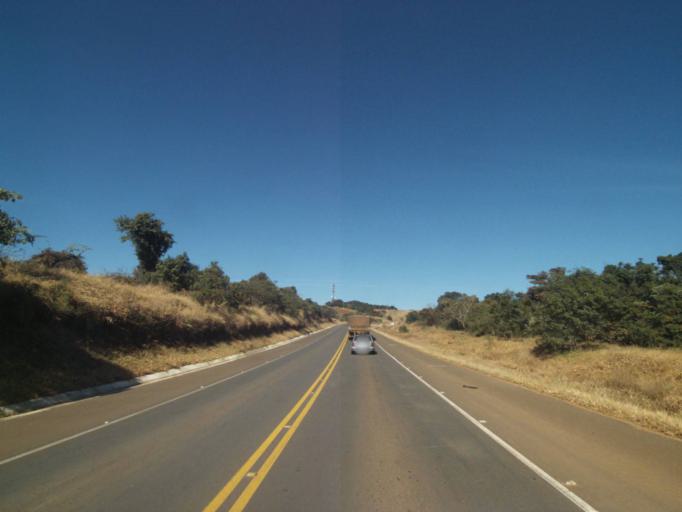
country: BR
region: Parana
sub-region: Tibagi
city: Tibagi
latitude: -24.7205
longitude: -50.4506
